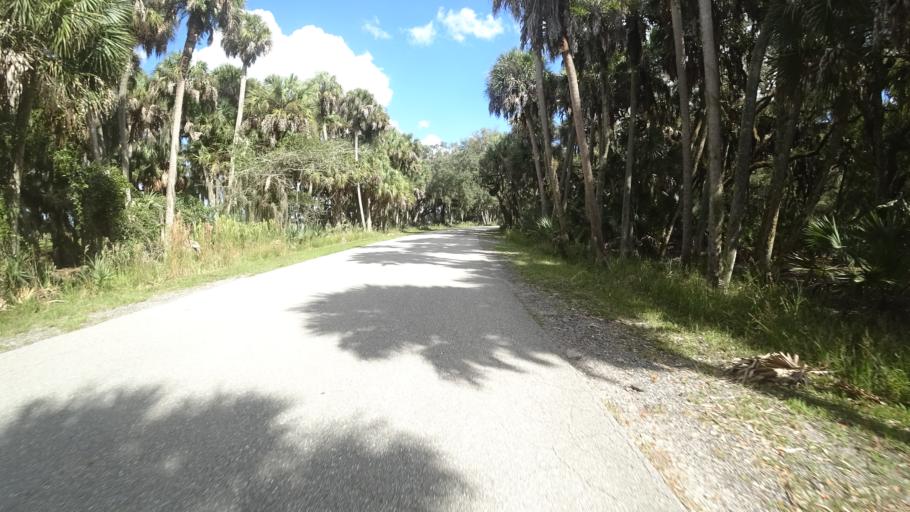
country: US
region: Florida
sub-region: Sarasota County
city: Lake Sarasota
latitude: 27.2522
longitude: -82.2932
